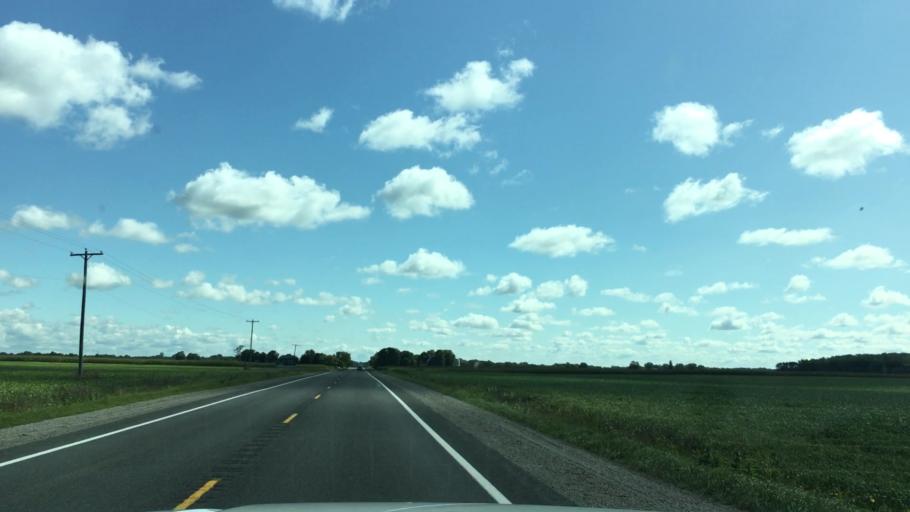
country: US
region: Michigan
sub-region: Montcalm County
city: Carson City
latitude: 43.1773
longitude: -84.8951
